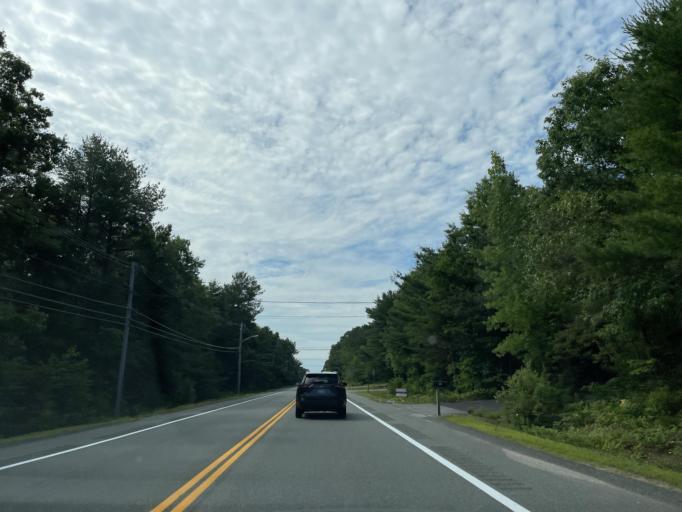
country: US
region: Rhode Island
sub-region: Kent County
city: West Greenwich
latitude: 41.6172
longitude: -71.6711
